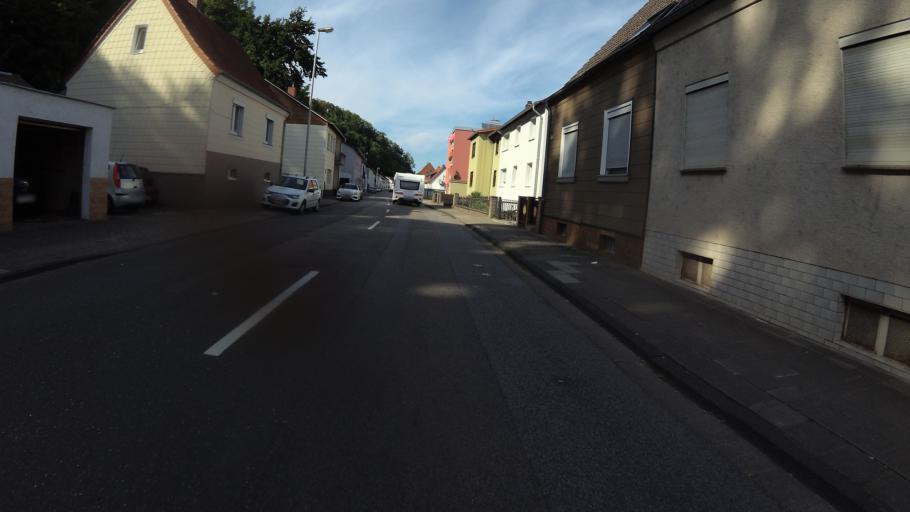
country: DE
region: Rheinland-Pfalz
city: Zweibrucken
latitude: 49.2341
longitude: 7.3555
